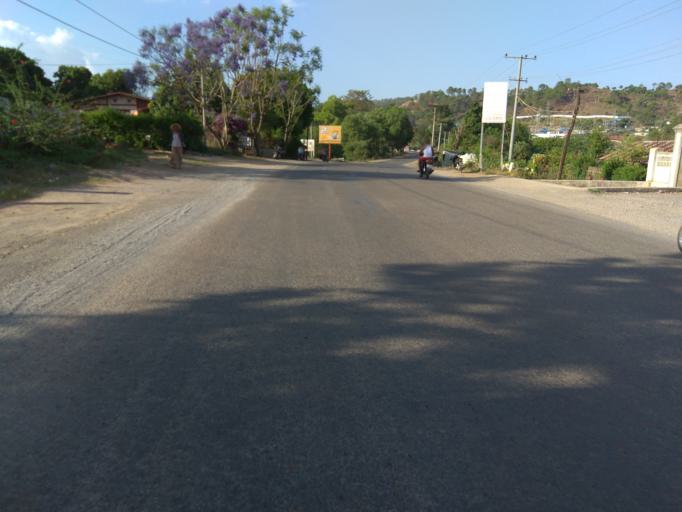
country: MM
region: Shan
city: Taunggyi
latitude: 20.6391
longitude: 96.5886
